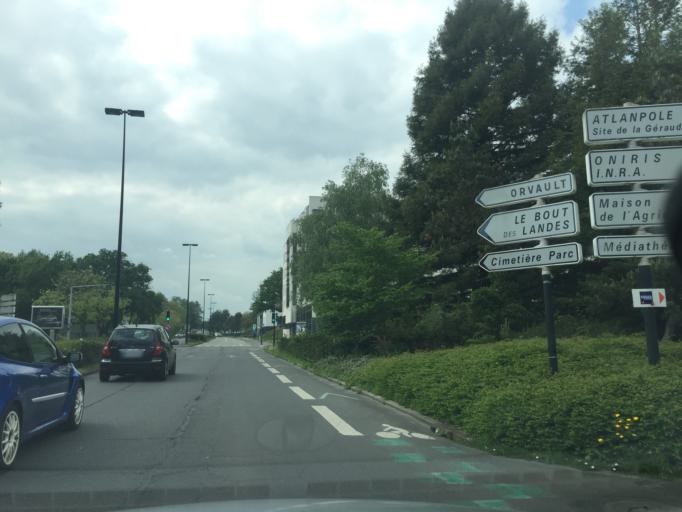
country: FR
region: Pays de la Loire
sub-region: Departement de la Loire-Atlantique
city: La Chapelle-sur-Erdre
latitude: 47.2624
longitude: -1.5666
